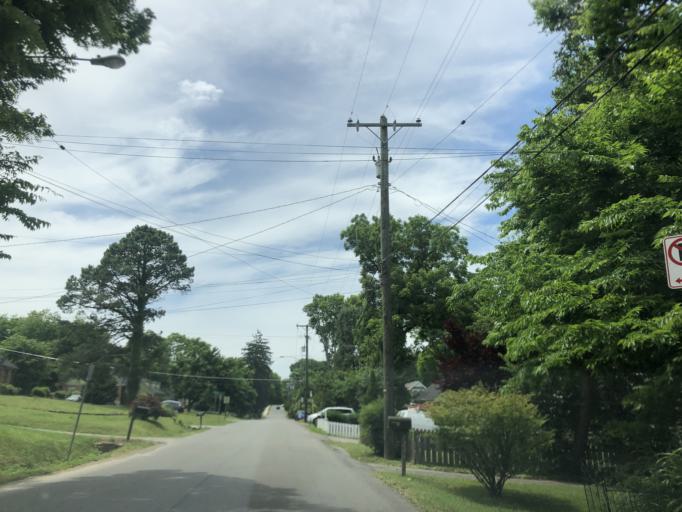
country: US
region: Tennessee
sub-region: Davidson County
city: Oak Hill
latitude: 36.1085
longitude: -86.7959
